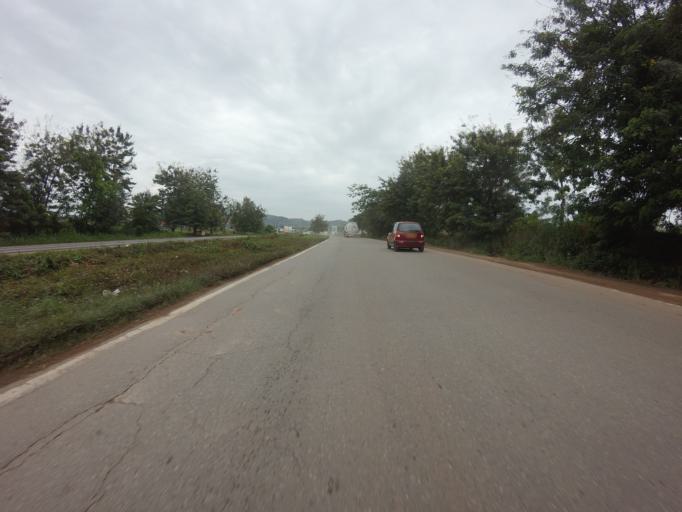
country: GH
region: Eastern
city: Nsawam
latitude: 5.7921
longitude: -0.3404
